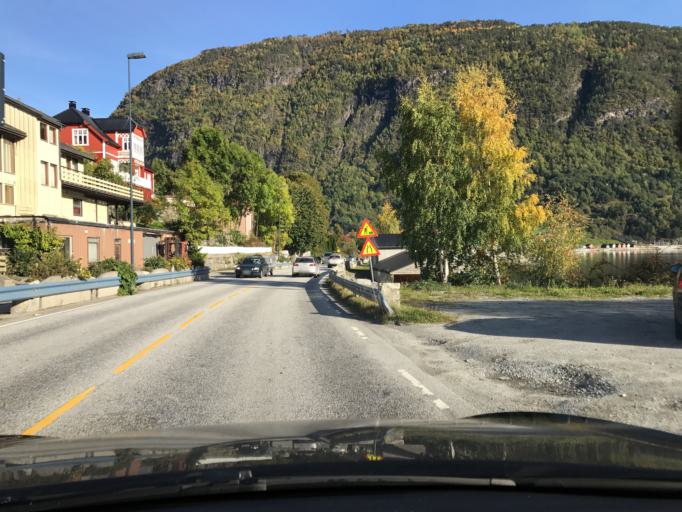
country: NO
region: Sogn og Fjordane
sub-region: Sogndal
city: Sogndalsfjora
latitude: 61.2322
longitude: 7.1113
